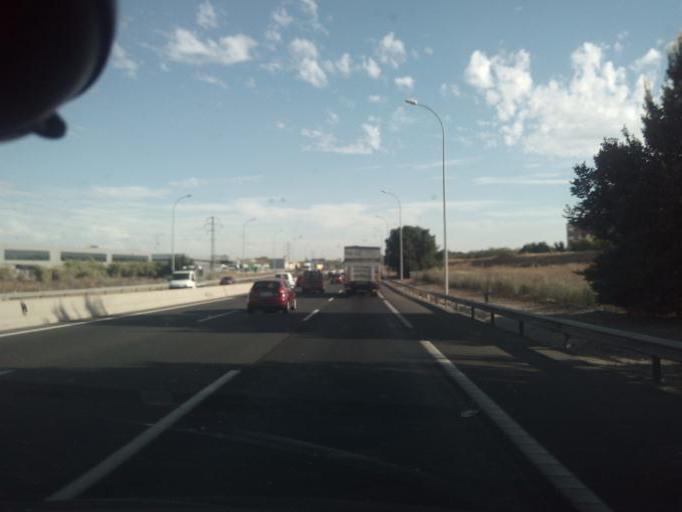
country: ES
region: Madrid
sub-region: Provincia de Madrid
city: Pinto
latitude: 40.2613
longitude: -3.6904
